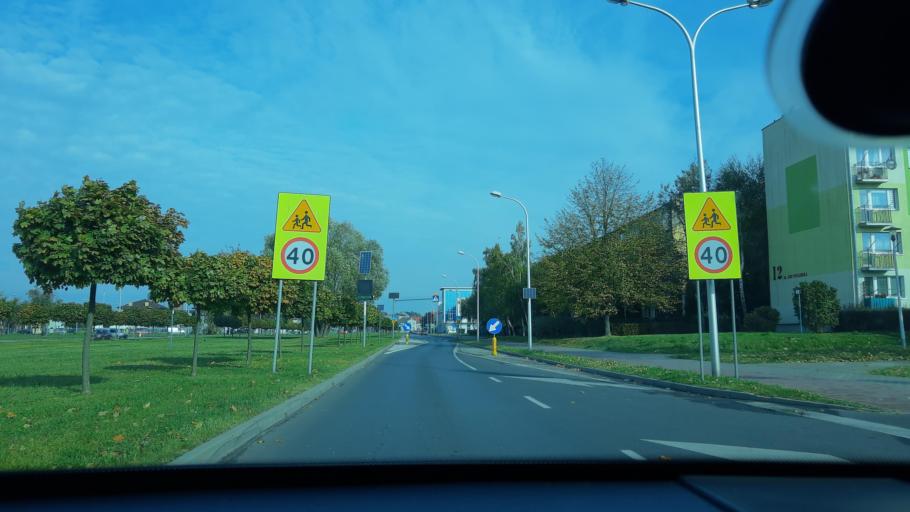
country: PL
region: Lodz Voivodeship
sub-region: Powiat sieradzki
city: Sieradz
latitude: 51.5917
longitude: 18.7151
